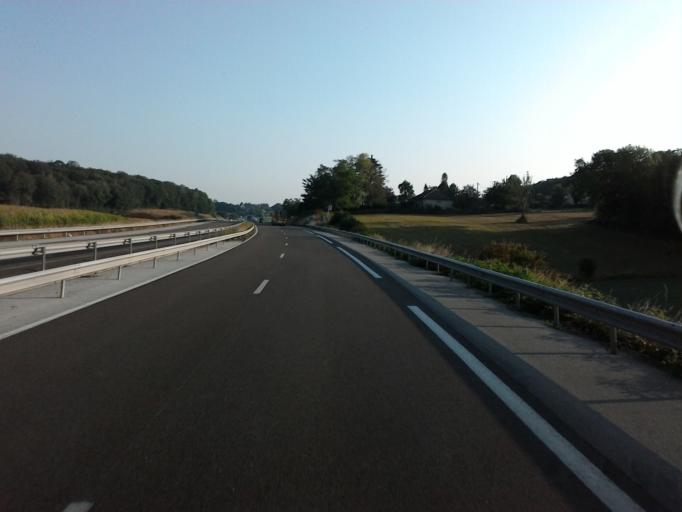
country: FR
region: Franche-Comte
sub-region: Departement de la Haute-Saone
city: Echenoz-la-Meline
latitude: 47.5678
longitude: 6.1400
